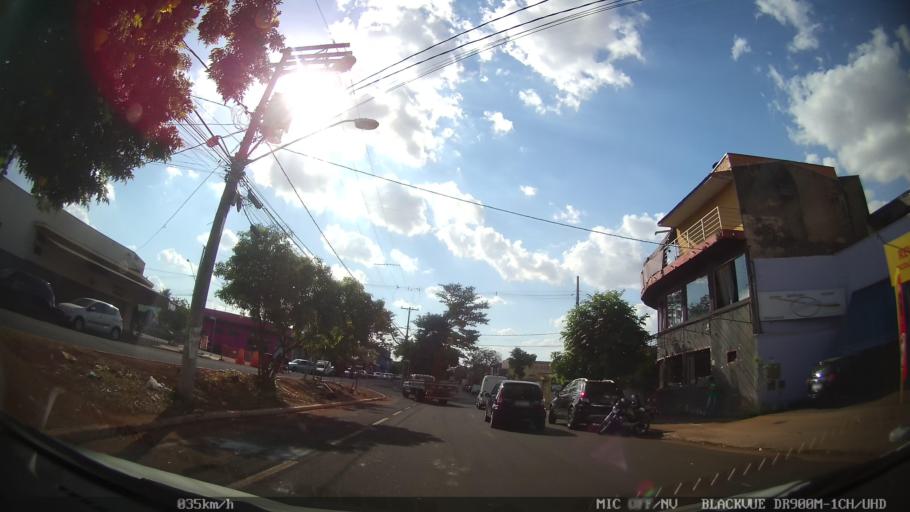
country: BR
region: Sao Paulo
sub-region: Ribeirao Preto
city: Ribeirao Preto
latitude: -21.1979
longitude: -47.8386
